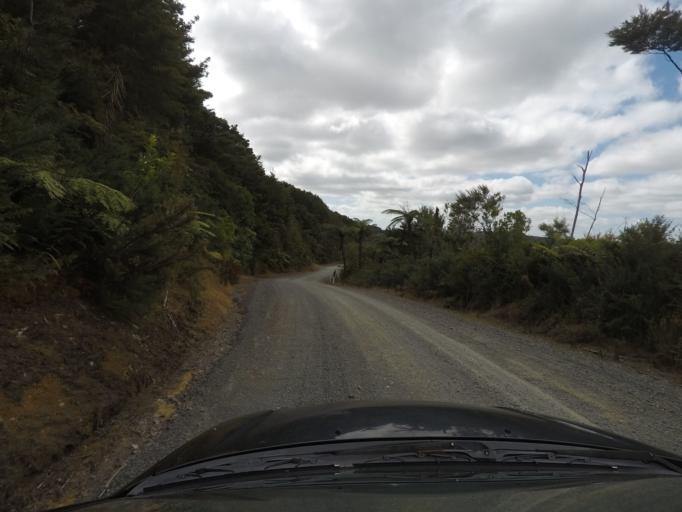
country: NZ
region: Northland
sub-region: Whangarei
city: Ruakaka
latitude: -35.9291
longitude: 174.3418
